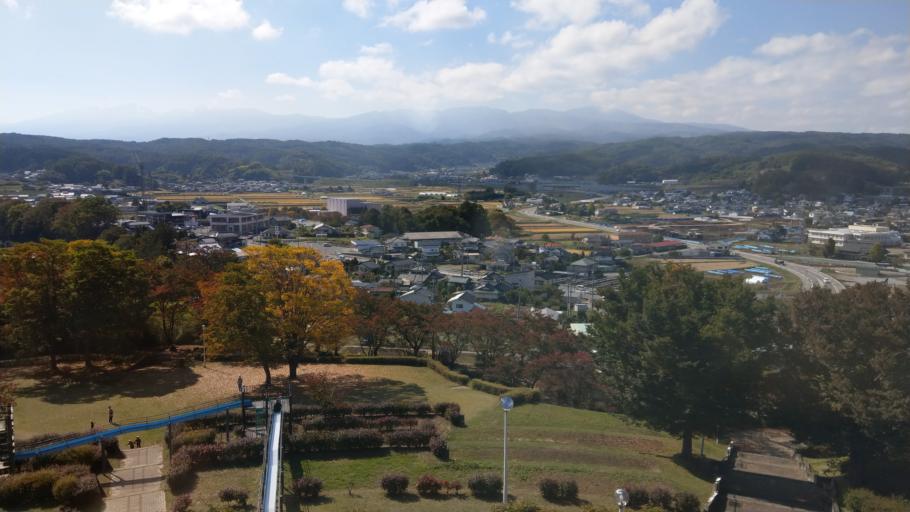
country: JP
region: Nagano
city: Saku
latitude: 36.1919
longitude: 138.4827
